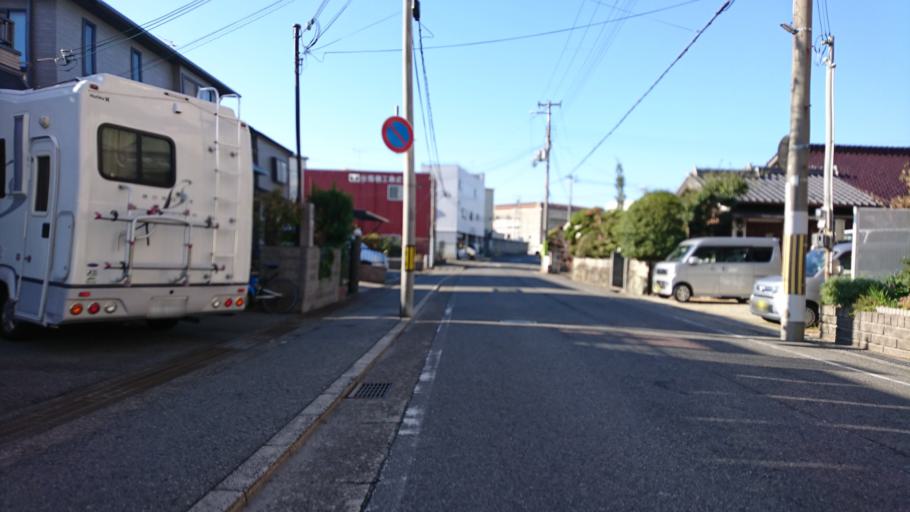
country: JP
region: Hyogo
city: Kakogawacho-honmachi
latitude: 34.7517
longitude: 134.8538
